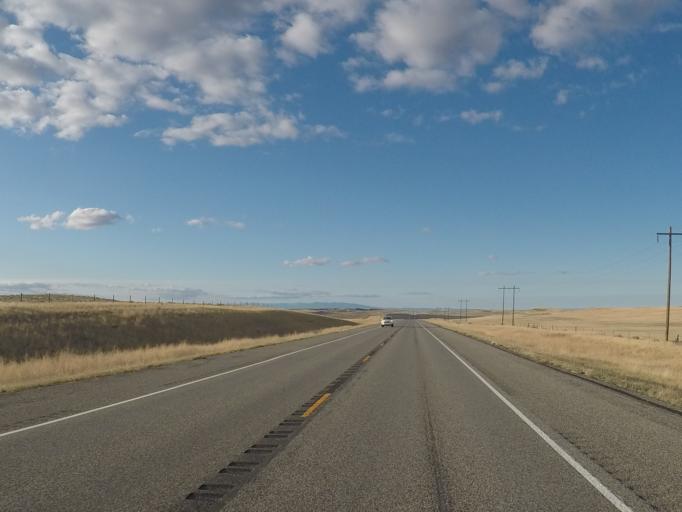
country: US
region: Montana
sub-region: Golden Valley County
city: Ryegate
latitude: 46.1797
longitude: -108.9098
